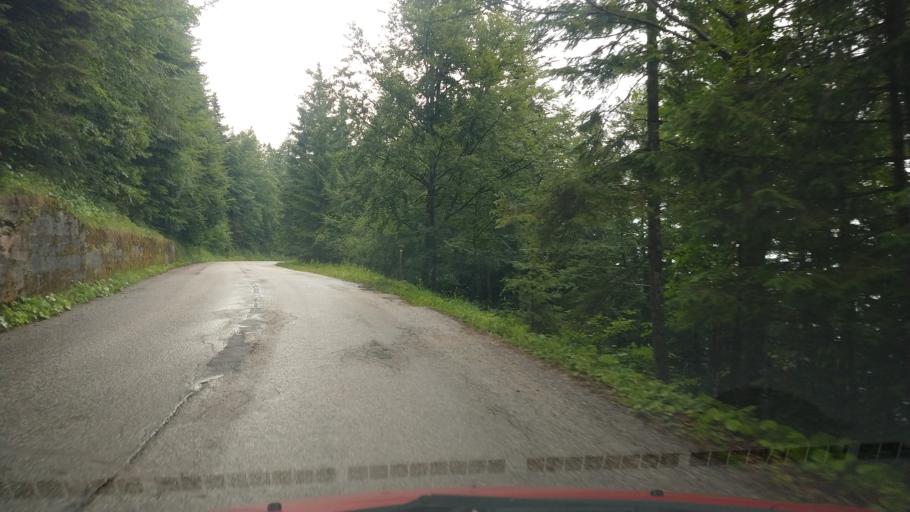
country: IT
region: Veneto
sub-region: Provincia di Vicenza
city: Lastebasse
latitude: 45.8936
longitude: 11.2728
